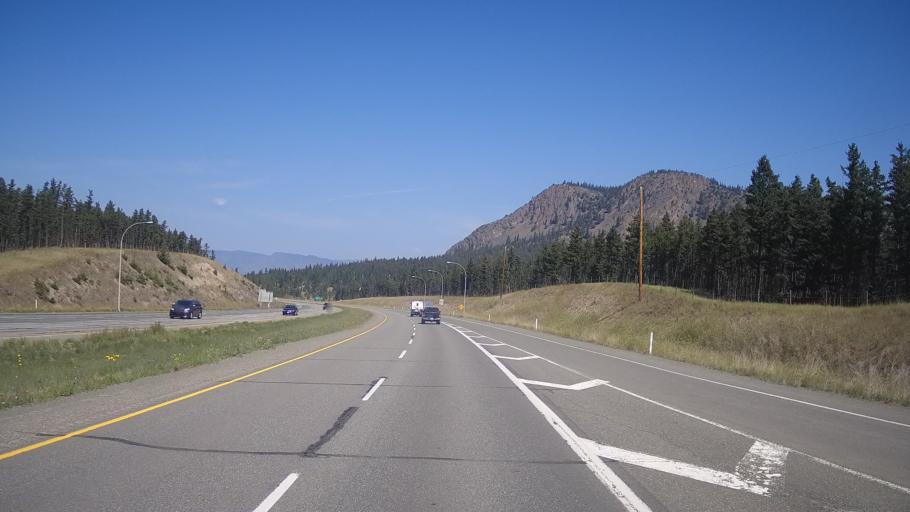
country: CA
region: British Columbia
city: Kamloops
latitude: 50.6215
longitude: -120.4720
